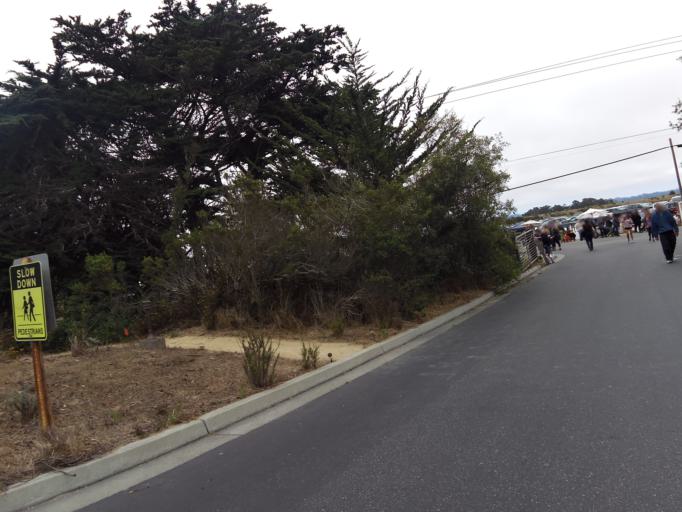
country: US
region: California
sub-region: Monterey County
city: Castroville
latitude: 36.7946
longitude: -121.7857
